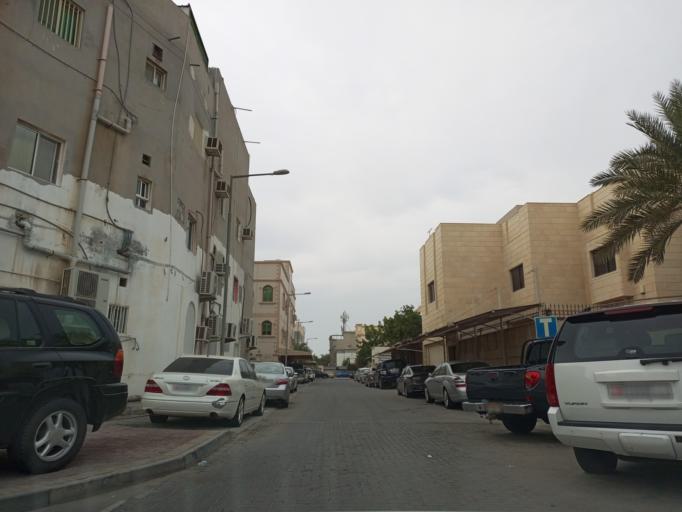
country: BH
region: Muharraq
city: Al Muharraq
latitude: 26.2600
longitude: 50.6315
